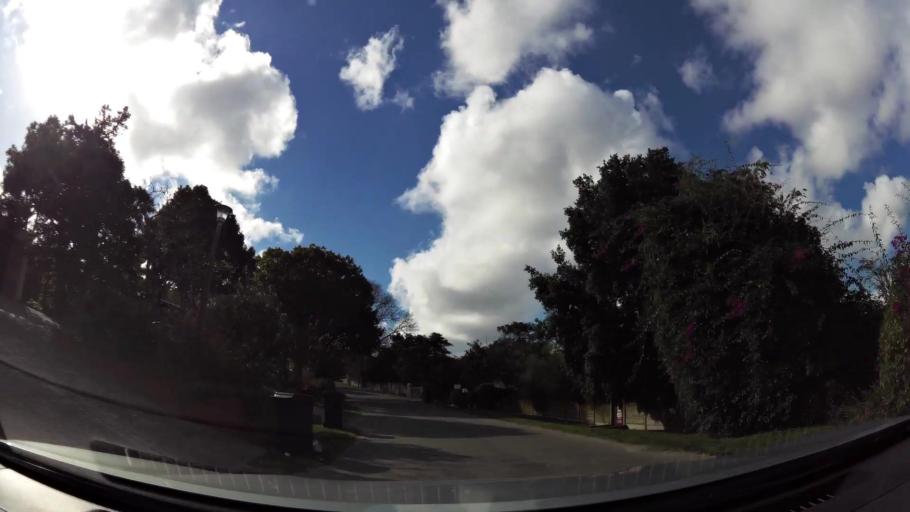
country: ZA
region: Western Cape
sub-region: Eden District Municipality
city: Knysna
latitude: -34.0377
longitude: 23.0707
